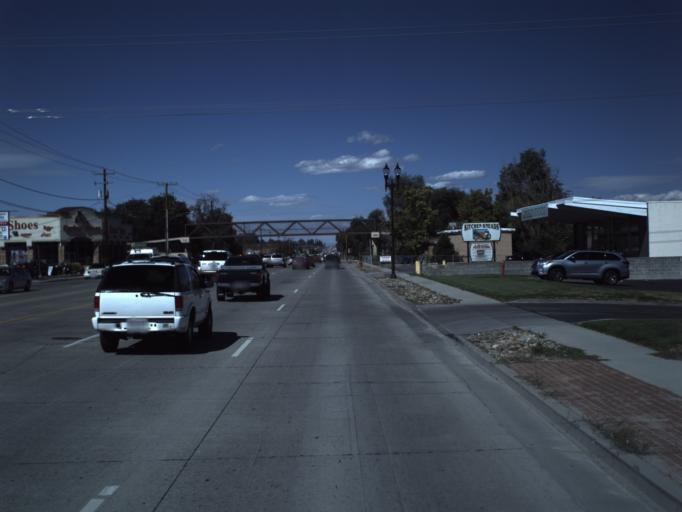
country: US
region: Utah
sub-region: Salt Lake County
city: West Jordan
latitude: 40.6126
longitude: -111.9386
